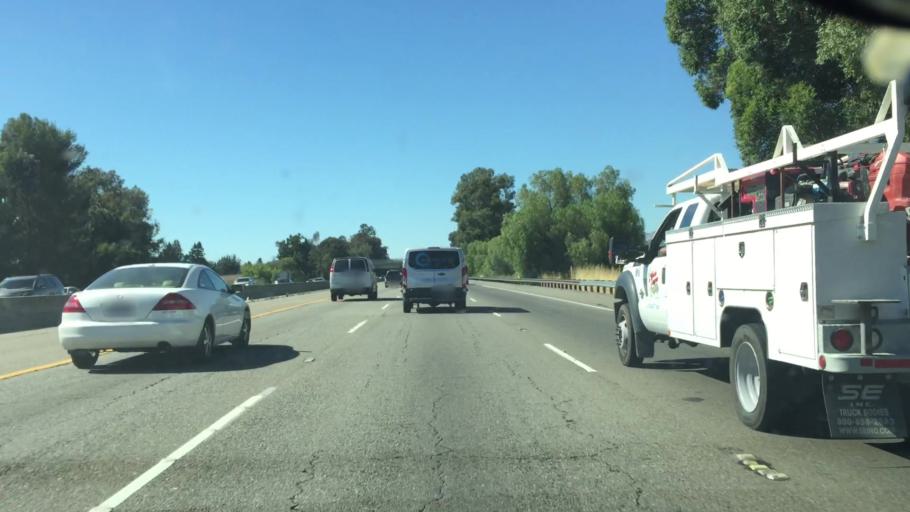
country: US
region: California
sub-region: Alameda County
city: Dublin
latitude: 37.6741
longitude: -121.9121
